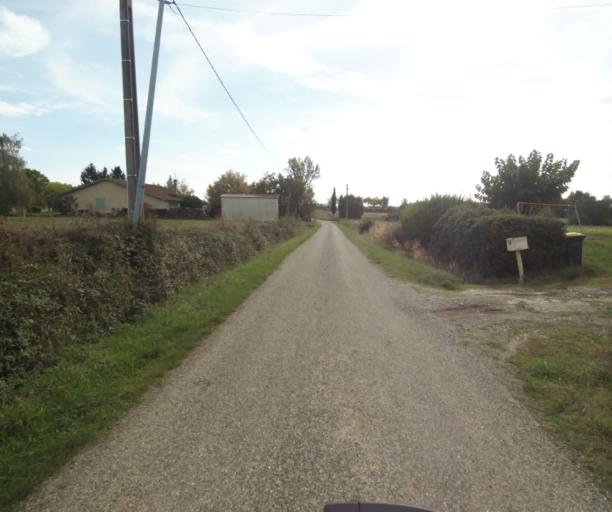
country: FR
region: Midi-Pyrenees
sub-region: Departement du Tarn-et-Garonne
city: Saint-Porquier
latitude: 43.9499
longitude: 1.1507
